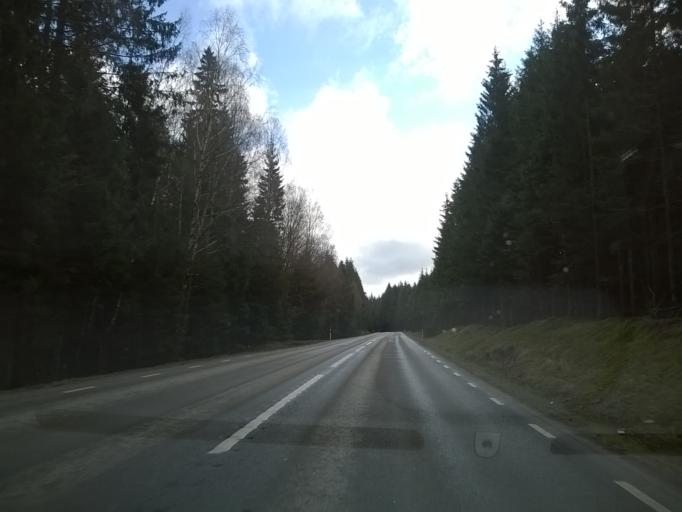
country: SE
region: Vaestra Goetaland
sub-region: Marks Kommun
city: Horred
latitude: 57.1567
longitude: 12.6574
